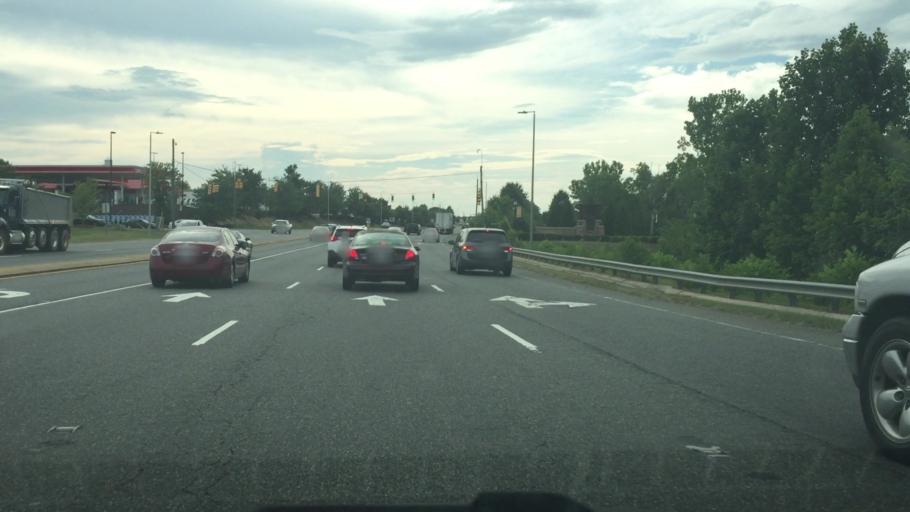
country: US
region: North Carolina
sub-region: Cabarrus County
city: Harrisburg
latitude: 35.3719
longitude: -80.7199
